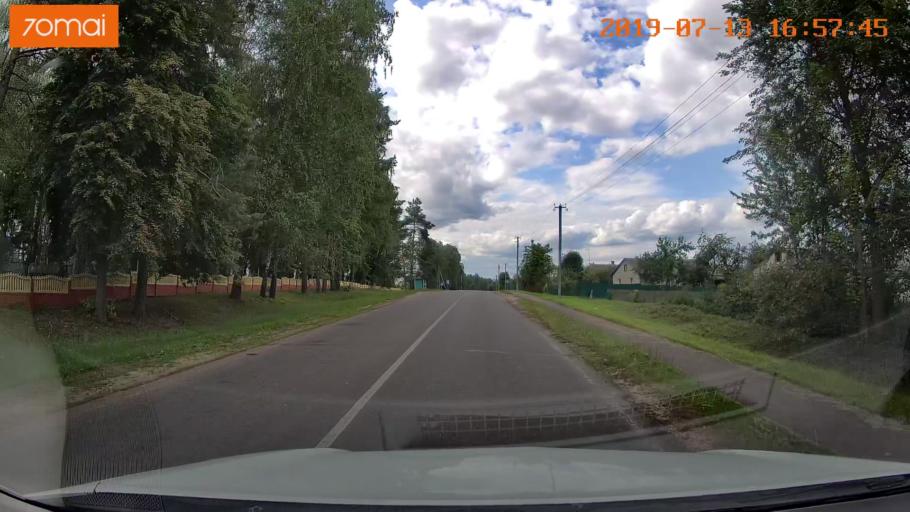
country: BY
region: Mogilev
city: Kirawsk
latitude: 53.2824
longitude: 29.4487
